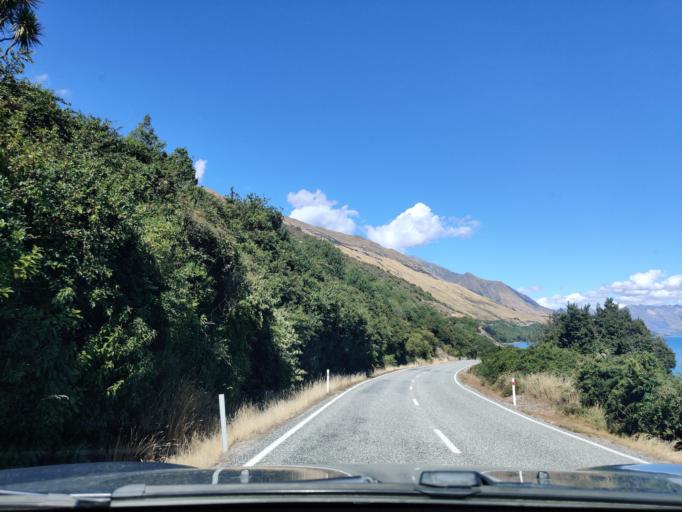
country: NZ
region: Otago
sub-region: Queenstown-Lakes District
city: Queenstown
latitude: -44.9426
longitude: 168.4324
